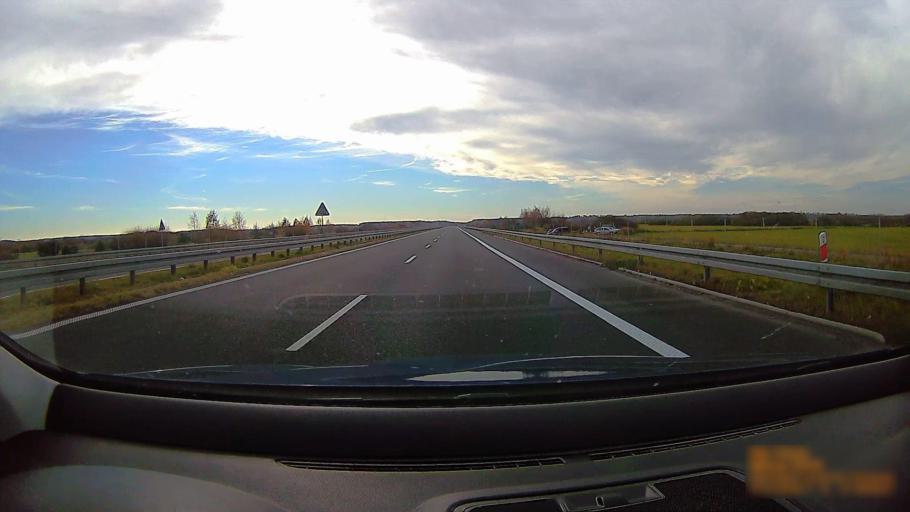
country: PL
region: Greater Poland Voivodeship
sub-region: Powiat ostrowski
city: Przygodzice
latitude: 51.5859
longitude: 17.8497
